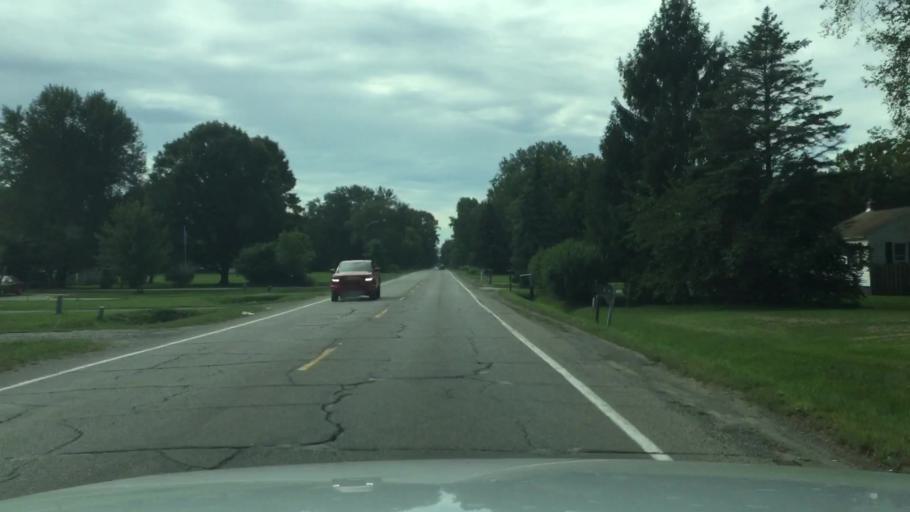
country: US
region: Michigan
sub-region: Wayne County
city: Belleville
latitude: 42.1722
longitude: -83.4828
